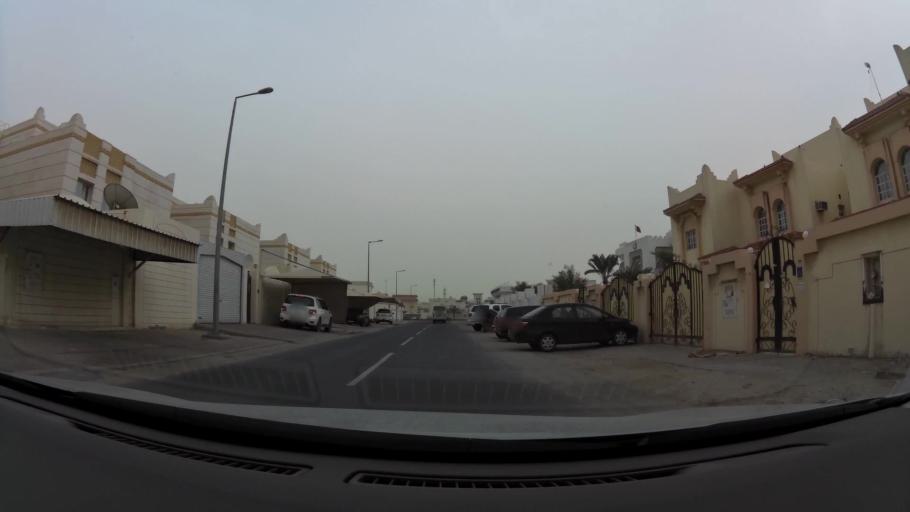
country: QA
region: Baladiyat ad Dawhah
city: Doha
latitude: 25.2525
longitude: 51.4853
